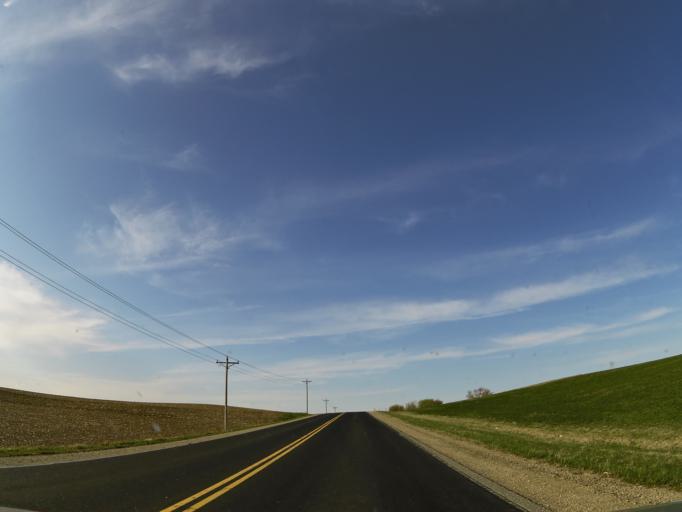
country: US
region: Wisconsin
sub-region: Pierce County
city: Ellsworth
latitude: 44.7251
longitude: -92.6089
